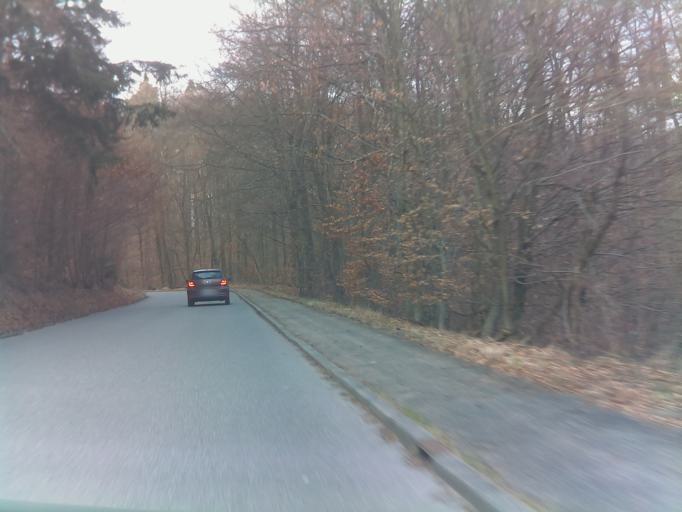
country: DE
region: Baden-Wuerttemberg
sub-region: Regierungsbezirk Stuttgart
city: Gerlingen
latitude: 48.7812
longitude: 9.0639
